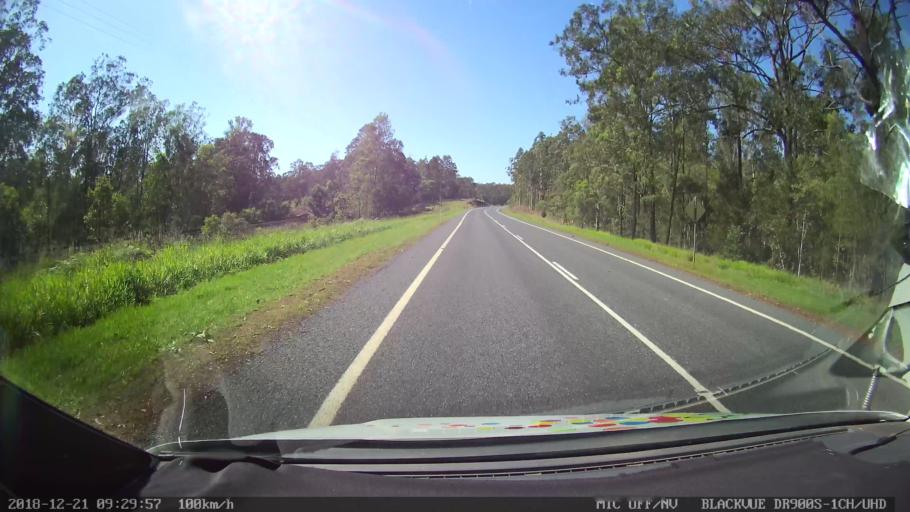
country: AU
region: New South Wales
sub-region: Clarence Valley
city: Maclean
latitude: -29.4392
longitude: 152.9911
